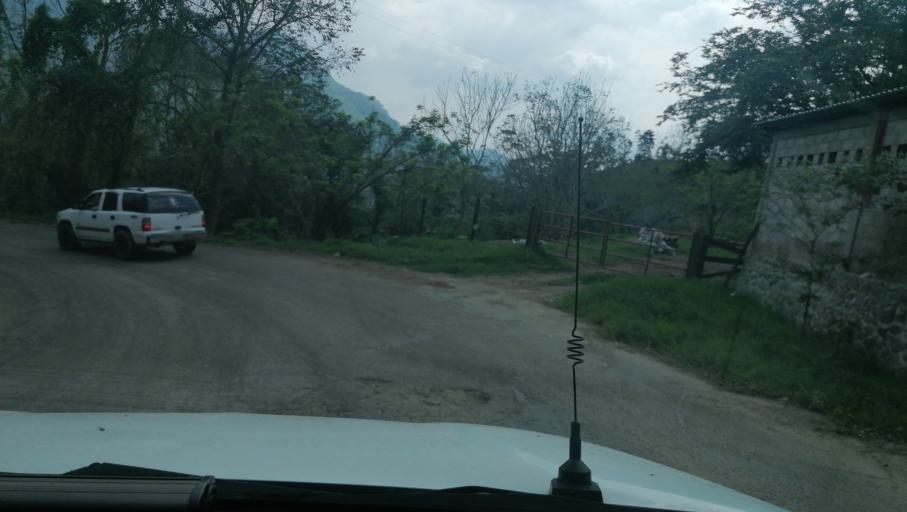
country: MX
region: Chiapas
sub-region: Francisco Leon
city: San Miguel la Sardina
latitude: 17.2251
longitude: -93.3461
